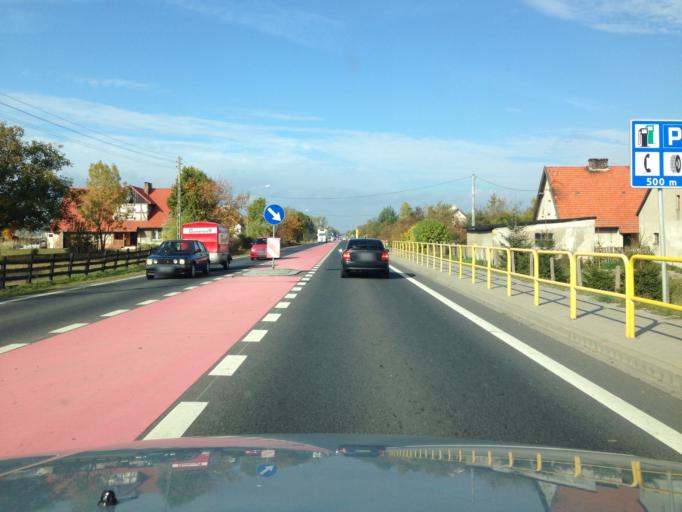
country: PL
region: Kujawsko-Pomorskie
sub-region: Powiat swiecki
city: Warlubie
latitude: 53.5583
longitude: 18.6520
